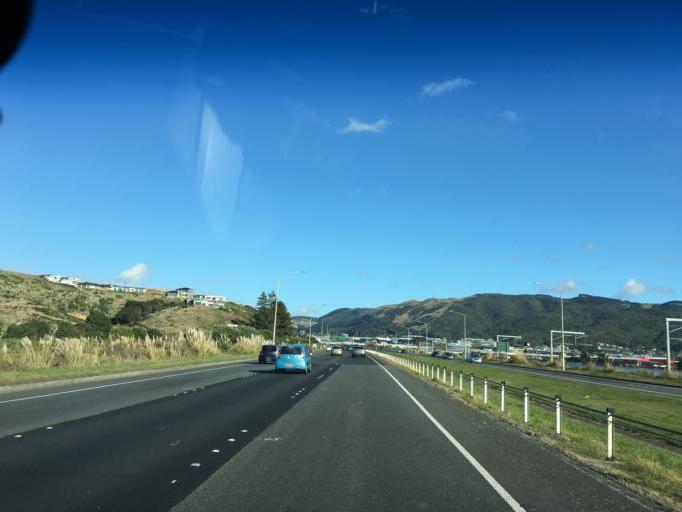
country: NZ
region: Wellington
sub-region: Porirua City
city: Porirua
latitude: -41.1250
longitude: 174.8488
